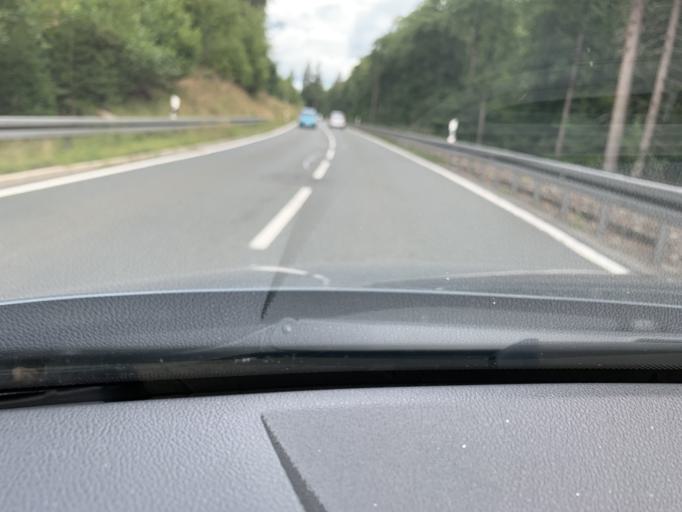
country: DE
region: Thuringia
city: Steinach
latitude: 50.4101
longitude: 11.1818
